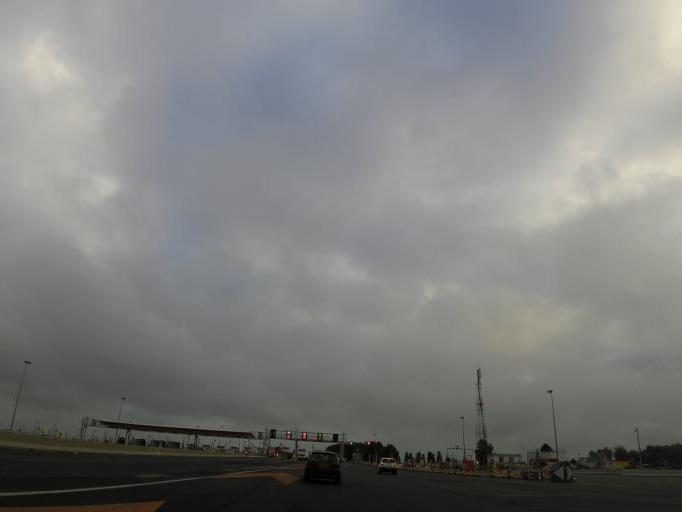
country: FR
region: Ile-de-France
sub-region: Departement de Seine-et-Marne
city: Bailly-Romainvilliers
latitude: 48.8523
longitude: 2.8372
